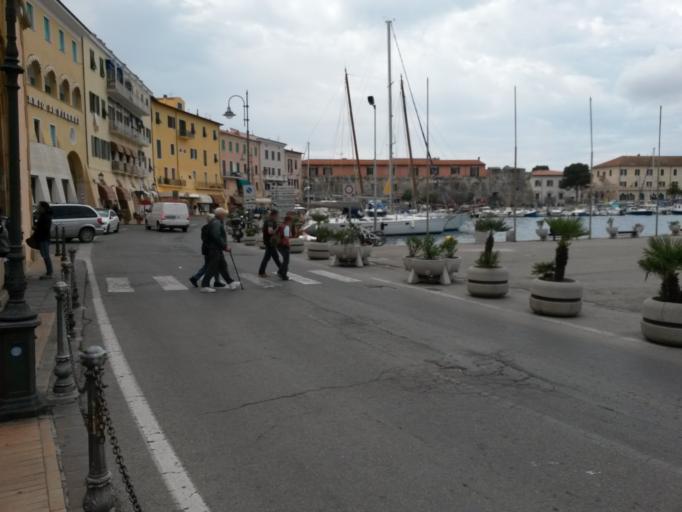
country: IT
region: Tuscany
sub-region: Provincia di Livorno
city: Portoferraio
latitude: 42.8145
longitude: 10.3310
